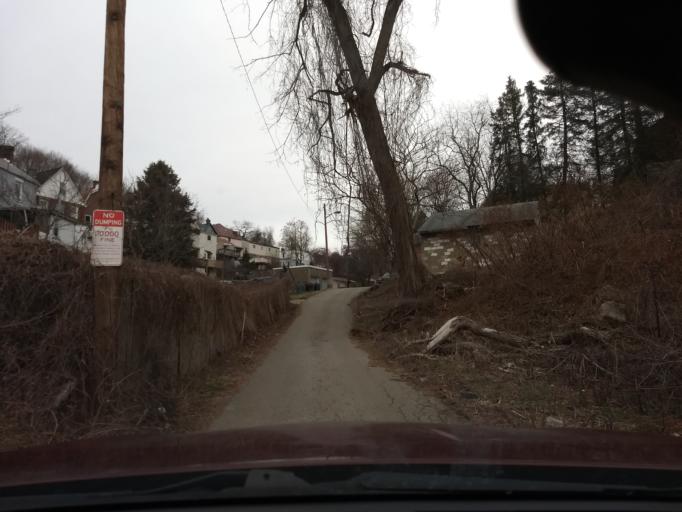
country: US
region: Pennsylvania
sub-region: Allegheny County
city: Homestead
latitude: 40.4171
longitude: -79.9370
